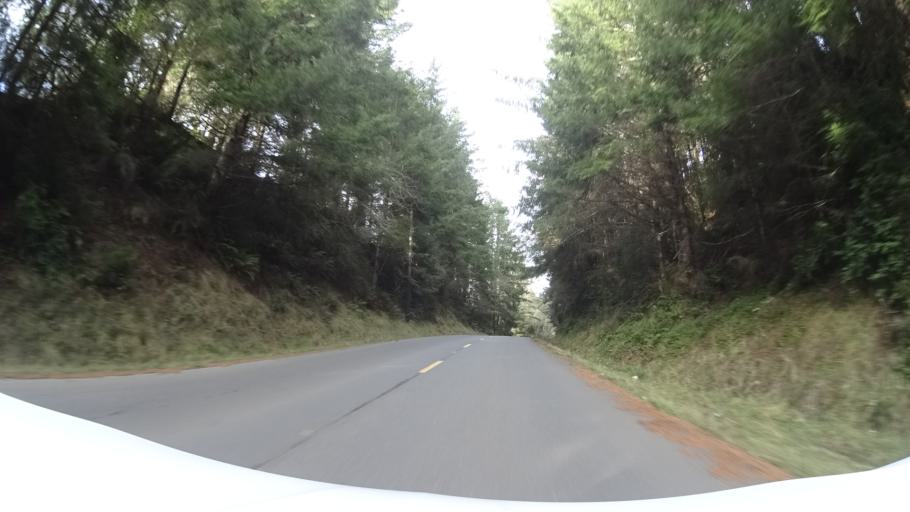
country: US
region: California
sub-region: Humboldt County
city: Ferndale
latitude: 40.5550
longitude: -124.2735
